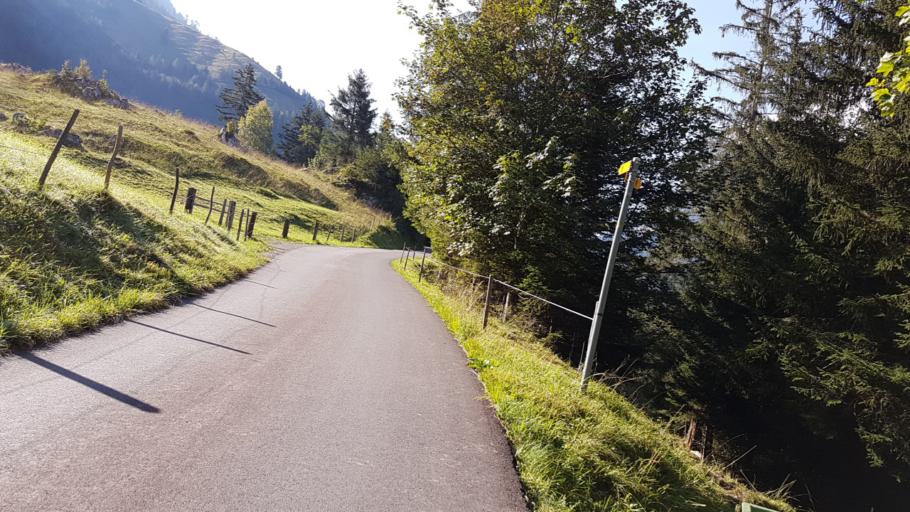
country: CH
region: Bern
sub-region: Frutigen-Niedersimmental District
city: Frutigen
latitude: 46.5530
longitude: 7.6706
